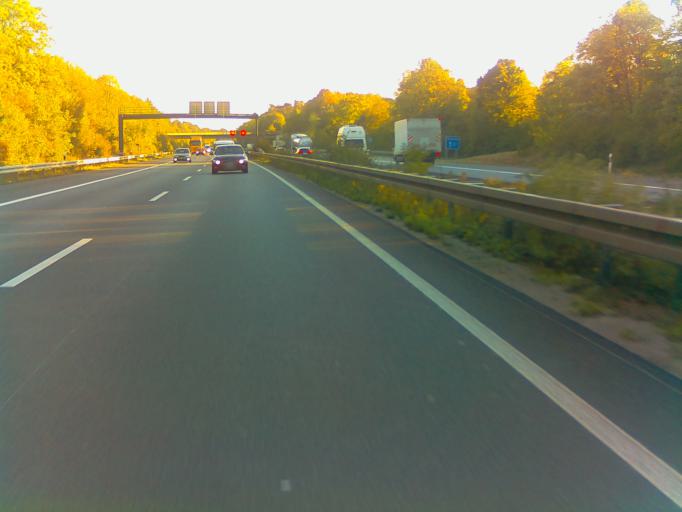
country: DE
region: Hesse
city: Pfungstadt
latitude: 49.7907
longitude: 8.6189
